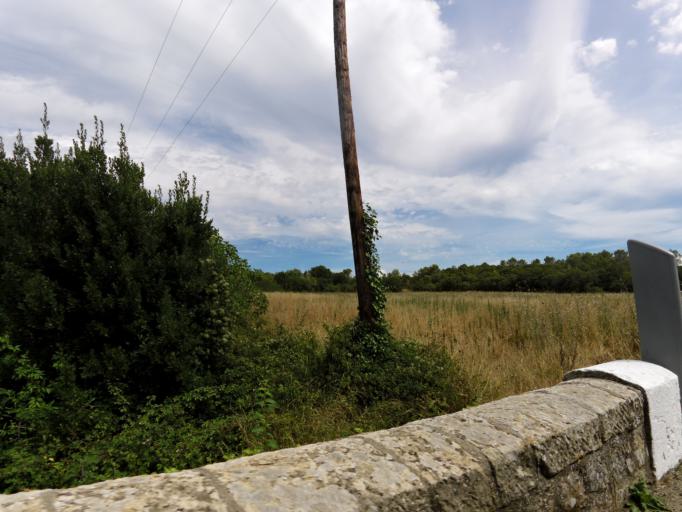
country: FR
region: Languedoc-Roussillon
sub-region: Departement du Gard
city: Congenies
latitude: 43.8175
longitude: 4.1477
